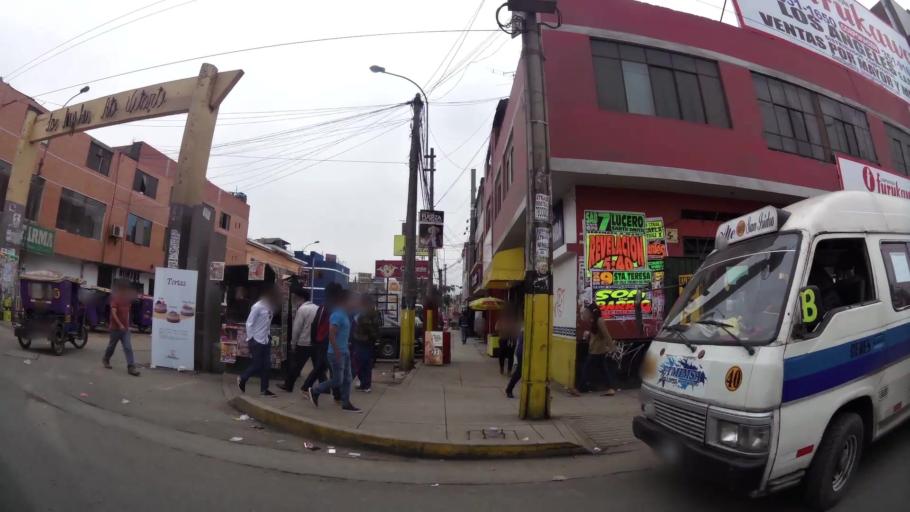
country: PE
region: Lima
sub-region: Lima
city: Vitarte
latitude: -12.0343
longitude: -76.9289
